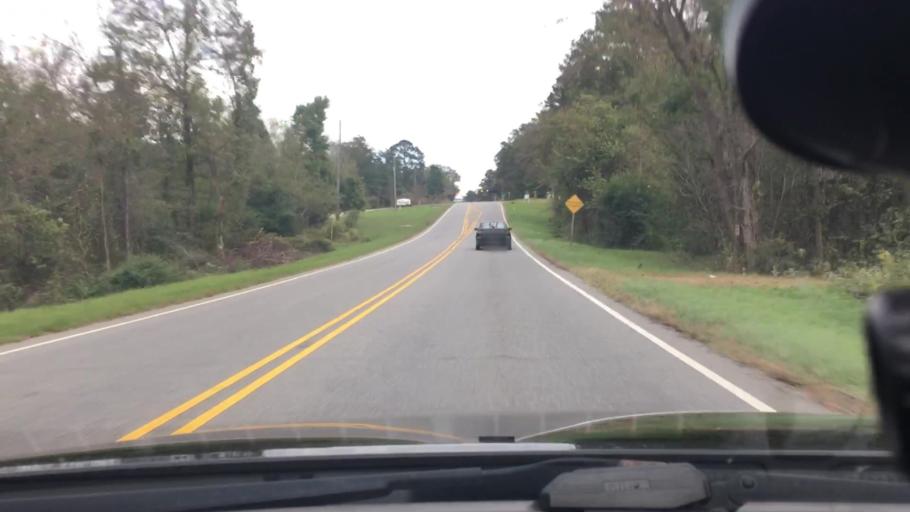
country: US
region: North Carolina
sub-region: Moore County
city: Robbins
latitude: 35.4044
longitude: -79.5799
